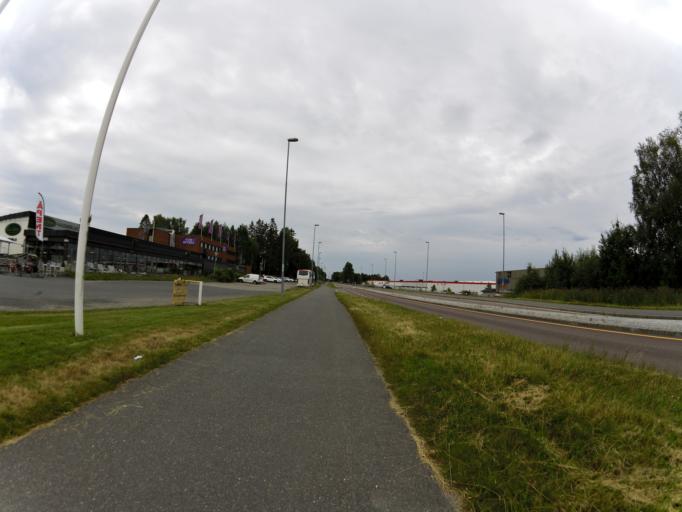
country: NO
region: Akershus
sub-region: Vestby
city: Vestby
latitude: 59.6184
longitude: 10.7401
